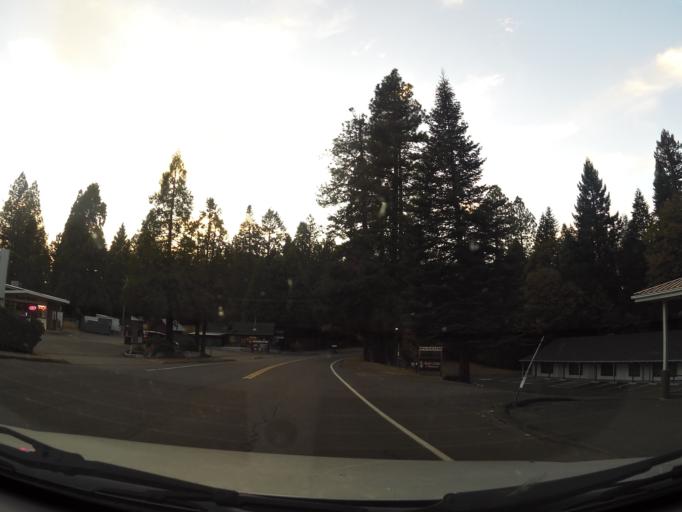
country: US
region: California
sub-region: El Dorado County
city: Pollock Pines
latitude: 38.7495
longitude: -120.6179
